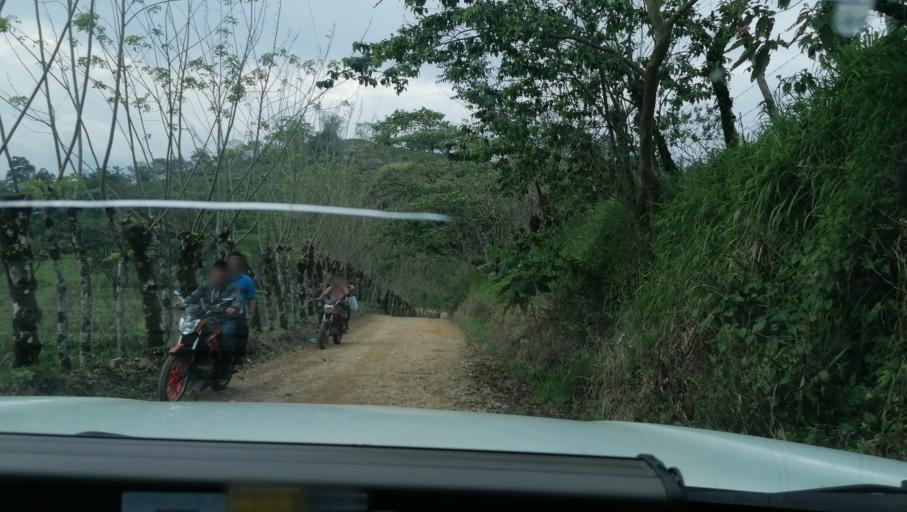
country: MX
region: Chiapas
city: Ixtacomitan
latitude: 17.3395
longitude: -93.1172
